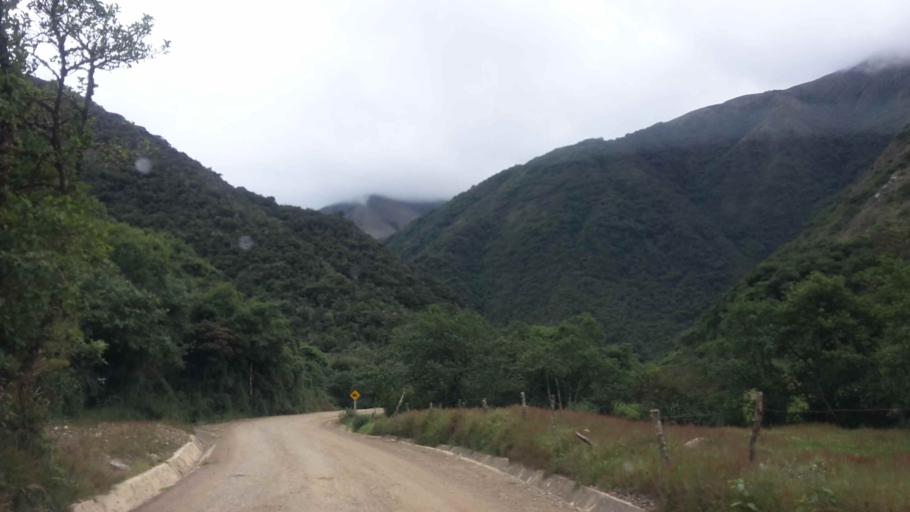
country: BO
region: Cochabamba
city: Totora
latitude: -17.5621
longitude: -65.2752
